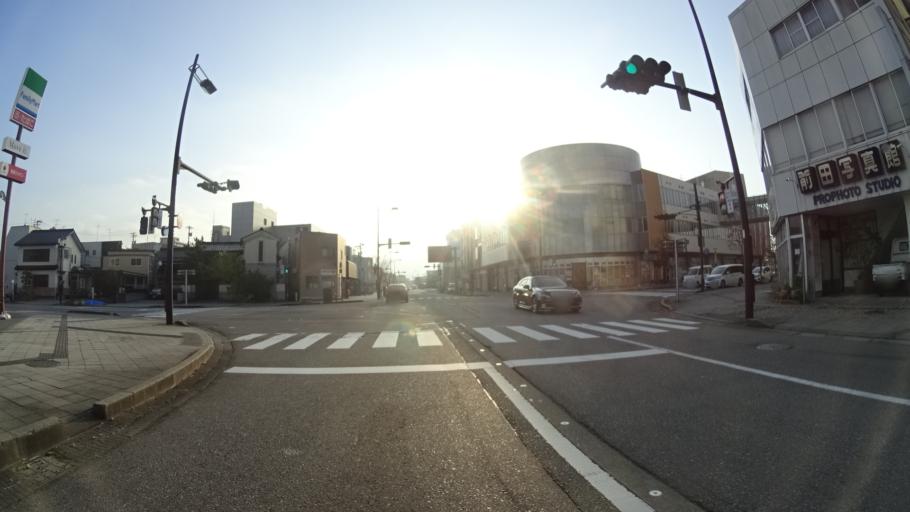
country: JP
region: Ishikawa
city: Nanao
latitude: 37.0440
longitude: 136.9638
